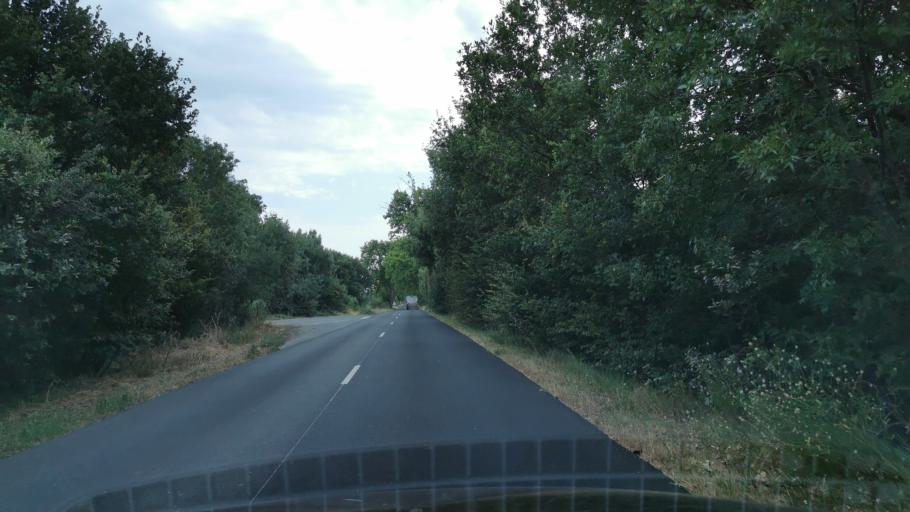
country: FR
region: Languedoc-Roussillon
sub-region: Departement de l'Herault
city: Capestang
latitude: 43.2886
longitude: 3.0240
